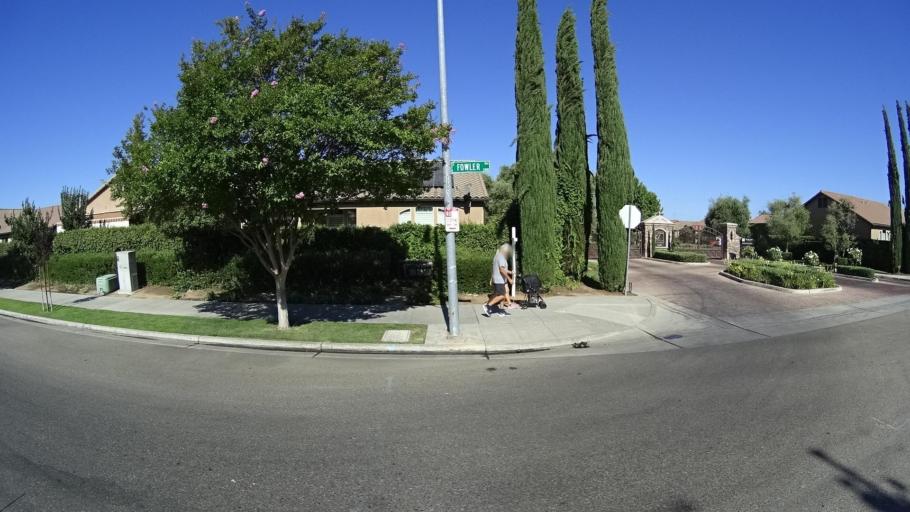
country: US
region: California
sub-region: Fresno County
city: Sunnyside
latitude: 36.7128
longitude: -119.6822
